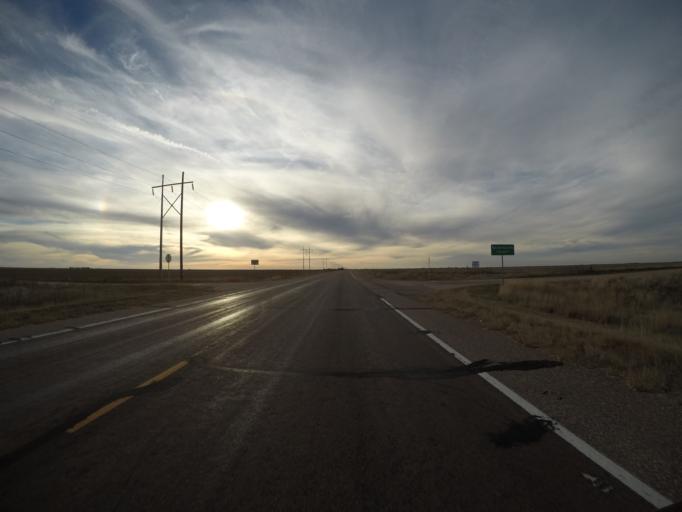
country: US
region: Colorado
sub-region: Yuma County
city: Yuma
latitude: 39.6549
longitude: -102.8018
